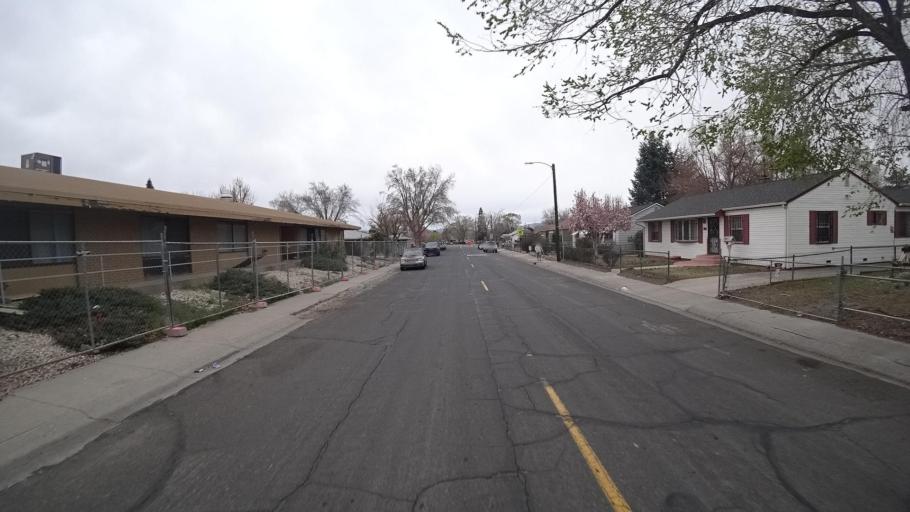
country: US
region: Nevada
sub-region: Washoe County
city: Reno
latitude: 39.5226
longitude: -119.7937
